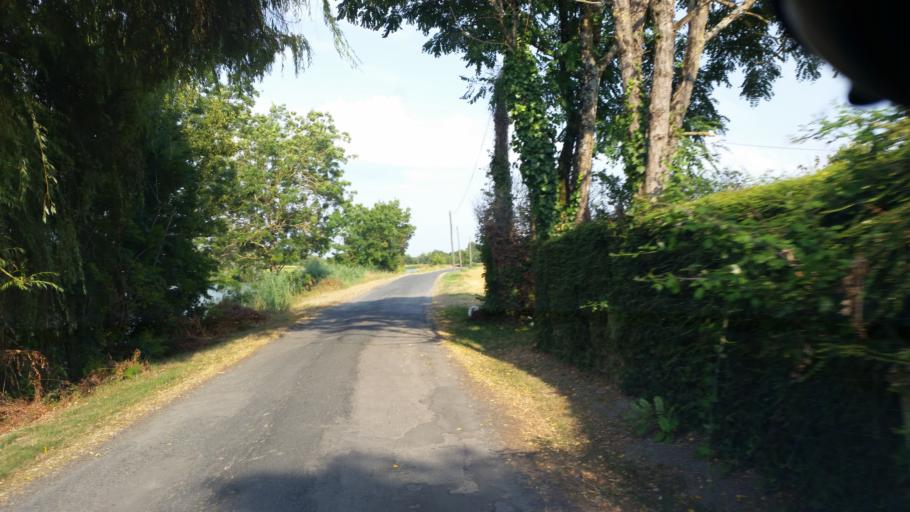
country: FR
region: Pays de la Loire
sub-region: Departement de la Vendee
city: Vix
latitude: 46.3242
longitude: -0.8862
